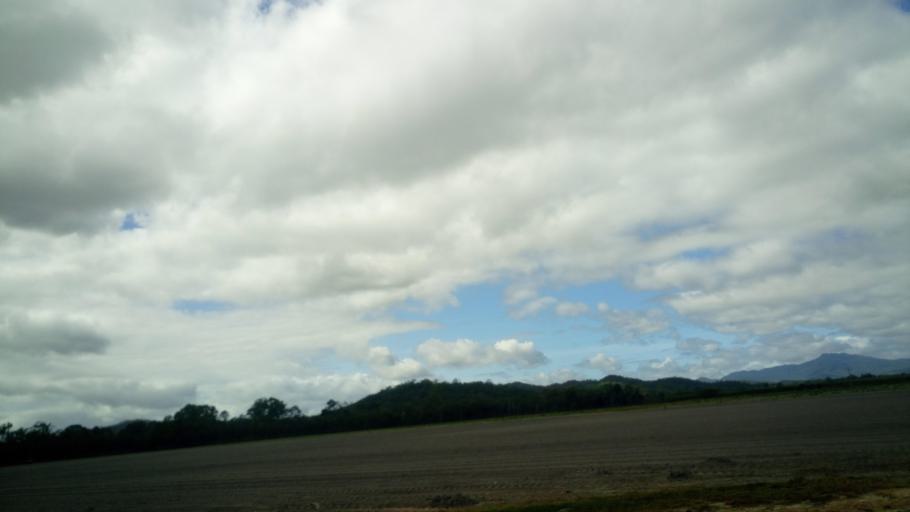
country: AU
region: Queensland
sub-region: Tablelands
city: Mareeba
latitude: -16.9673
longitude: 145.4565
